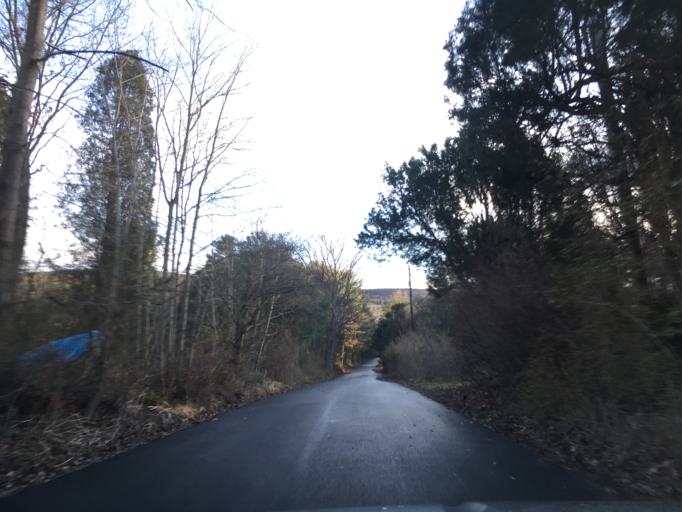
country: US
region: Pennsylvania
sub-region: Carbon County
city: Lehighton
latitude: 40.7771
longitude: -75.7108
